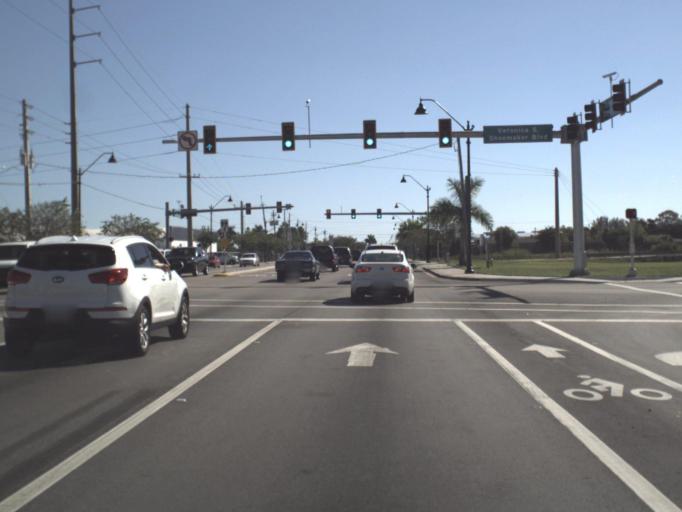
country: US
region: Florida
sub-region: Lee County
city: Fort Myers
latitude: 26.6410
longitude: -81.8411
